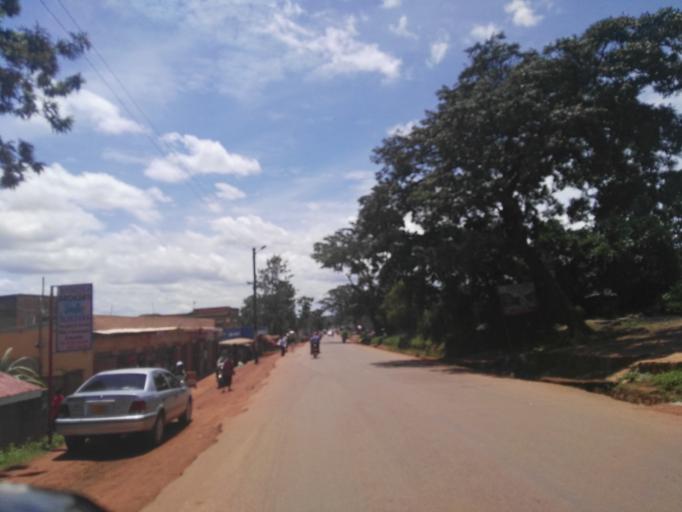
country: UG
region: Central Region
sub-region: Kampala District
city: Kampala
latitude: 0.2830
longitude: 32.5763
